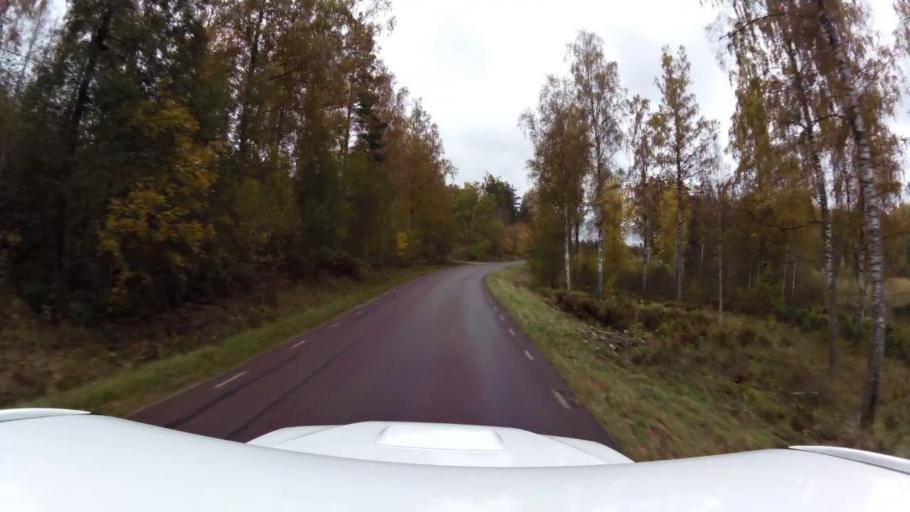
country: SE
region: OEstergoetland
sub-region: Linkopings Kommun
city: Ljungsbro
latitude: 58.5697
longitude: 15.5143
